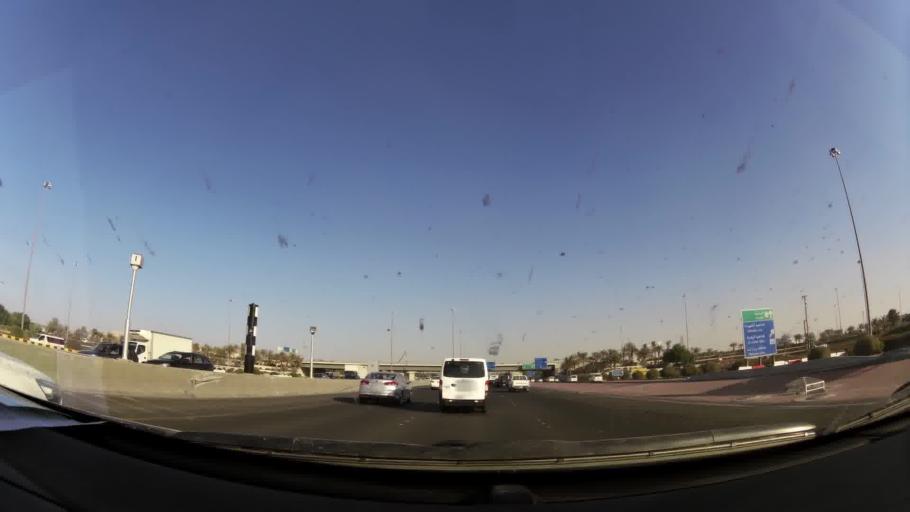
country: KW
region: Al Farwaniyah
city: Janub as Surrah
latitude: 29.2643
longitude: 48.0104
